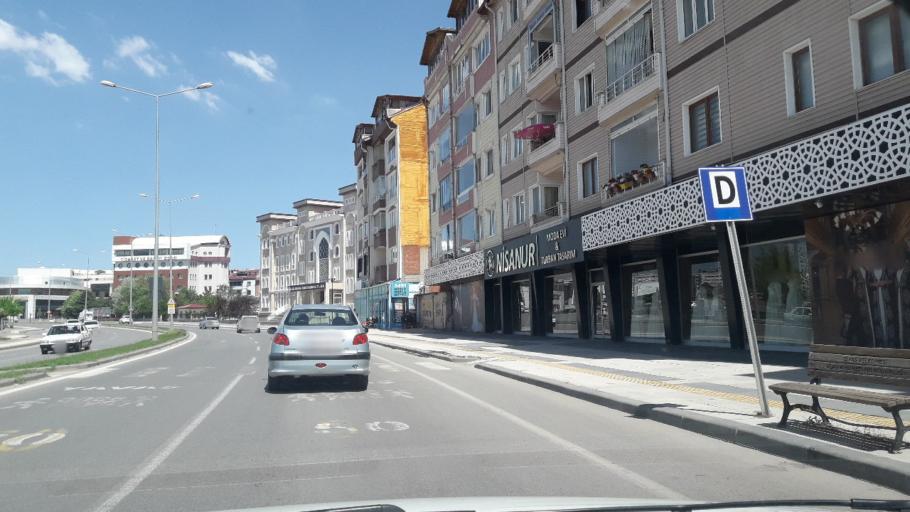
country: TR
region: Sivas
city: Sivas
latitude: 39.7405
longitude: 37.0151
